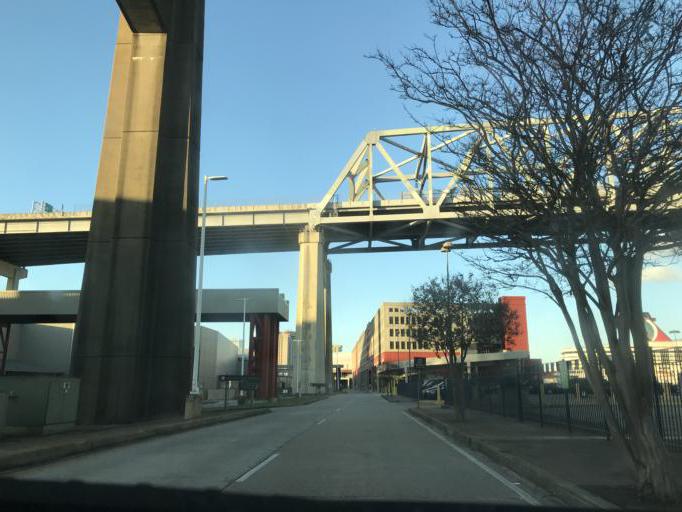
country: US
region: Louisiana
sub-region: Orleans Parish
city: New Orleans
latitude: 29.9375
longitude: -90.0617
